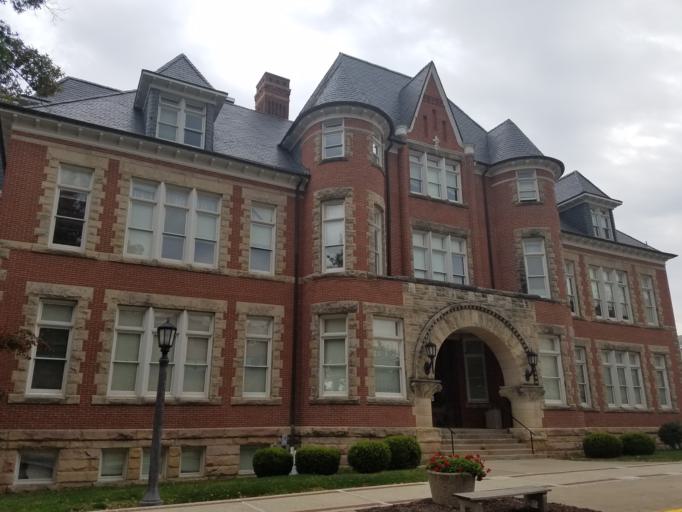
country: US
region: Pennsylvania
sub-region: Clarion County
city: Clarion
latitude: 41.2114
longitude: -79.3806
